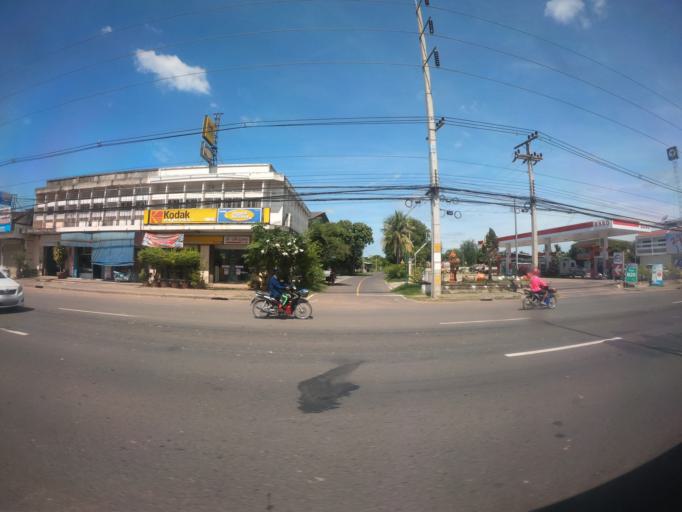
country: TH
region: Surin
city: Prasat
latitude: 14.6357
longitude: 103.4067
